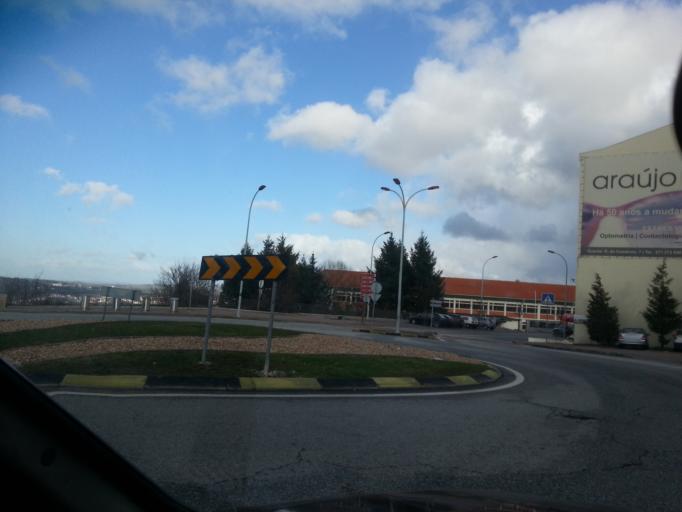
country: PT
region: Guarda
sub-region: Guarda
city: Guarda
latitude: 40.5429
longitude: -7.2651
